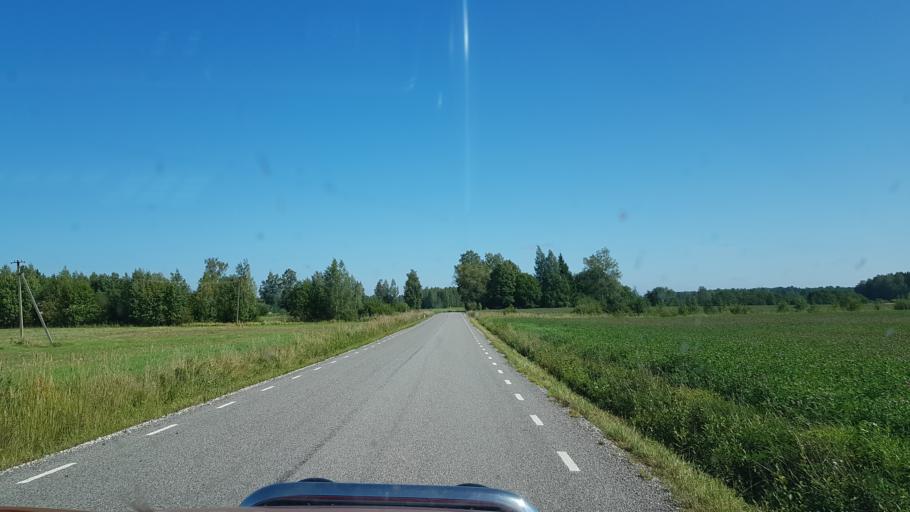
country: EE
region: Polvamaa
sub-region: Polva linn
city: Polva
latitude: 58.2148
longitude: 27.1855
